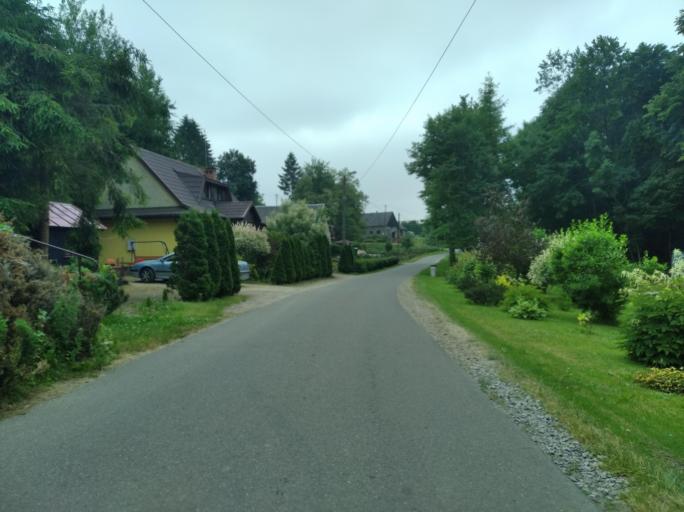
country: PL
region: Subcarpathian Voivodeship
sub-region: Powiat brzozowski
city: Haczow
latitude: 49.6770
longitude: 21.8926
